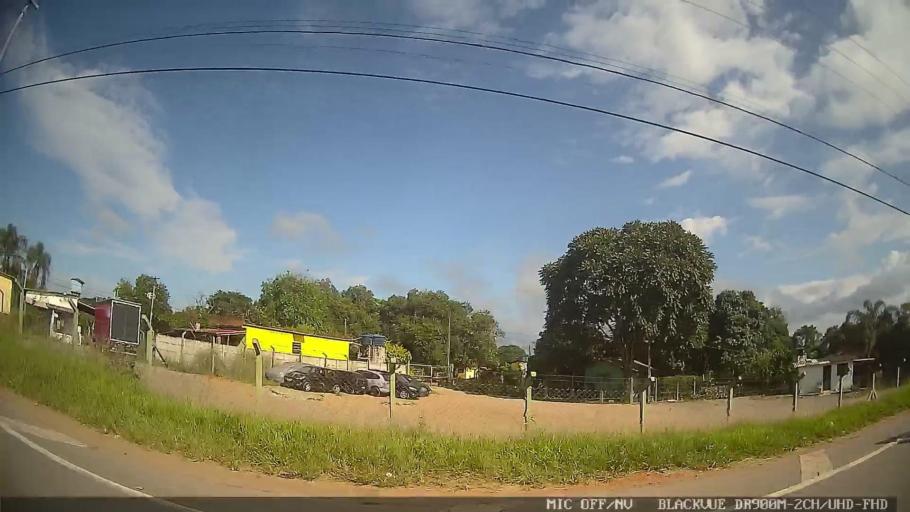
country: BR
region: Sao Paulo
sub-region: Jarinu
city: Jarinu
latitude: -23.0531
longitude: -46.6780
